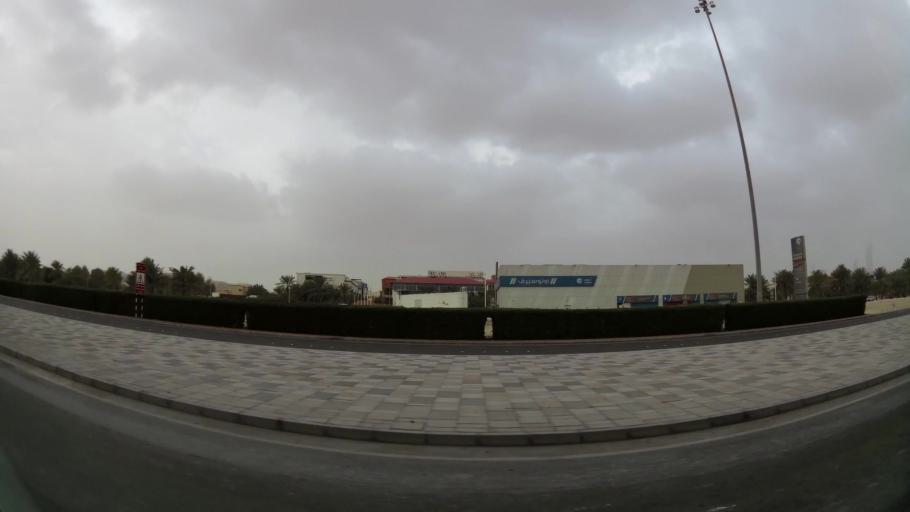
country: AE
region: Abu Dhabi
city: Abu Dhabi
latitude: 24.4765
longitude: 54.3896
